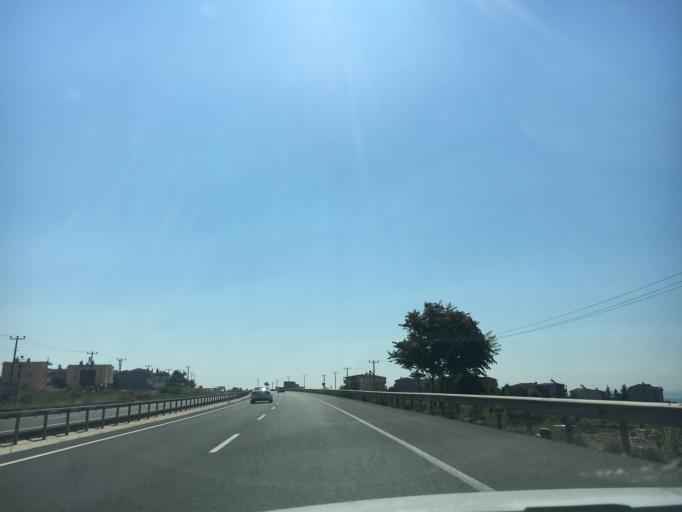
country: TR
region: Tekirdag
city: Marmara Ereglisi
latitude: 40.9702
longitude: 27.8857
